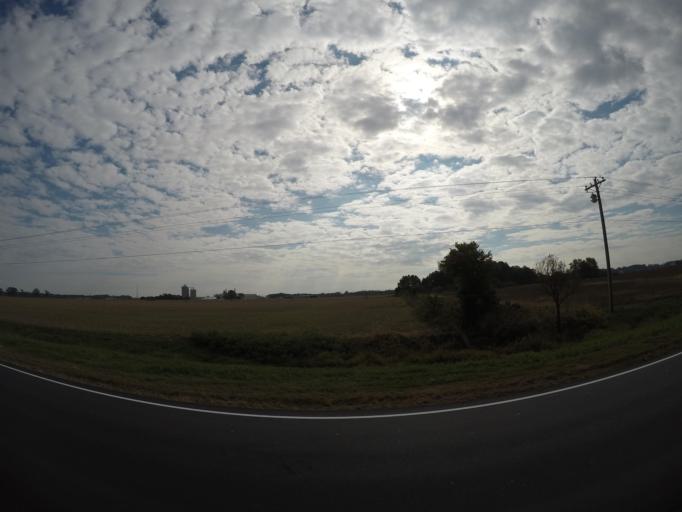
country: US
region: Delaware
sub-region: Sussex County
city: Bridgeville
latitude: 38.7610
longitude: -75.6176
